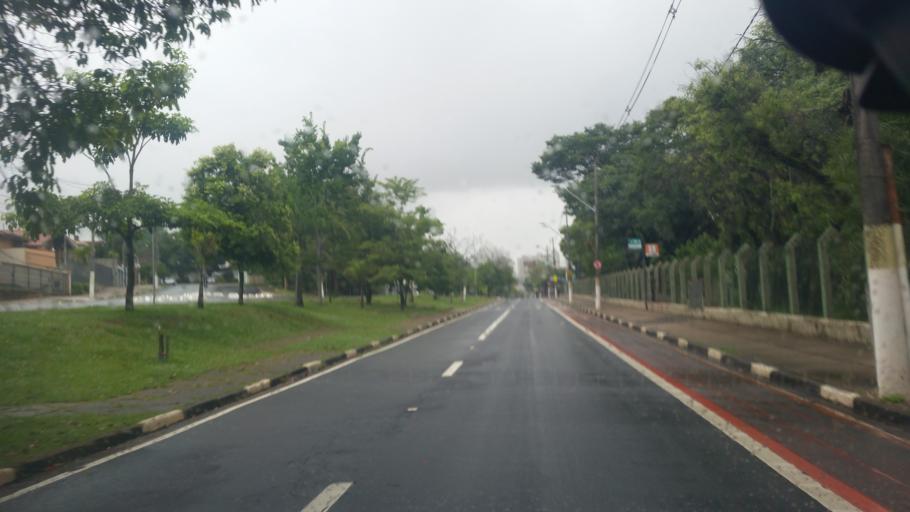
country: BR
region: Sao Paulo
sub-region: Campinas
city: Campinas
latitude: -22.8771
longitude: -47.0560
